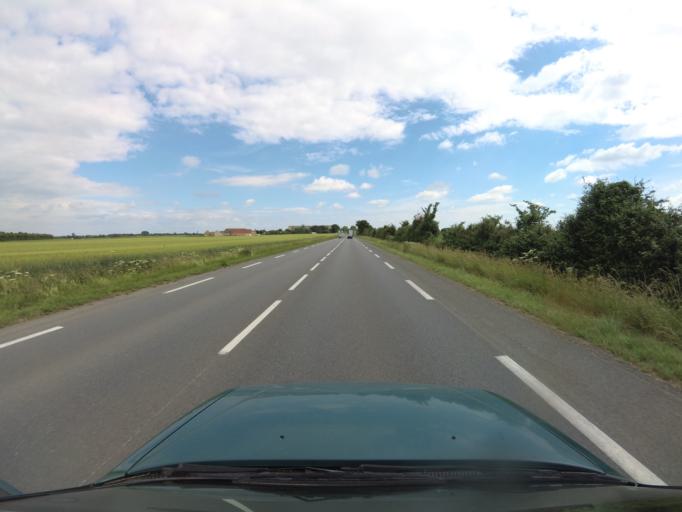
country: FR
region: Pays de la Loire
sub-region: Departement de la Vendee
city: Sainte-Gemme-la-Plaine
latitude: 46.4553
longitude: -1.1052
